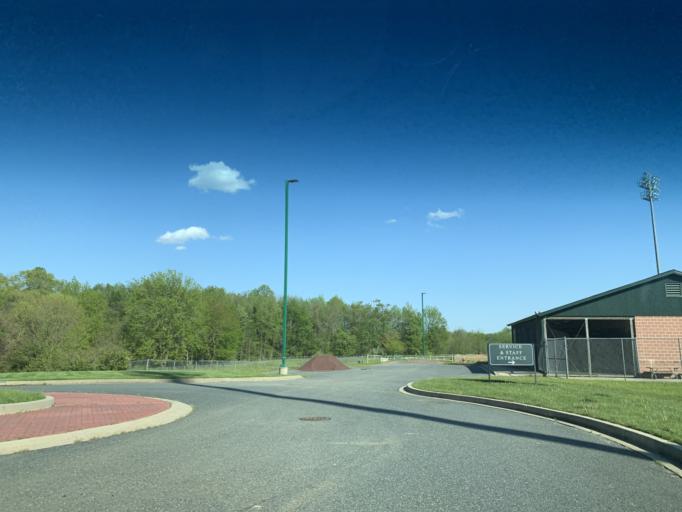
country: US
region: Maryland
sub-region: Harford County
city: Aberdeen
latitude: 39.5317
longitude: -76.1852
